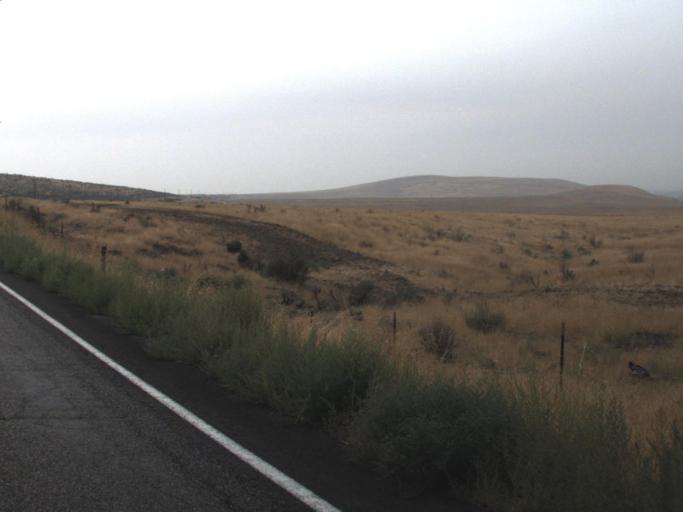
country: US
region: Washington
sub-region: Yakima County
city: Sunnyside
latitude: 46.4355
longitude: -119.9372
